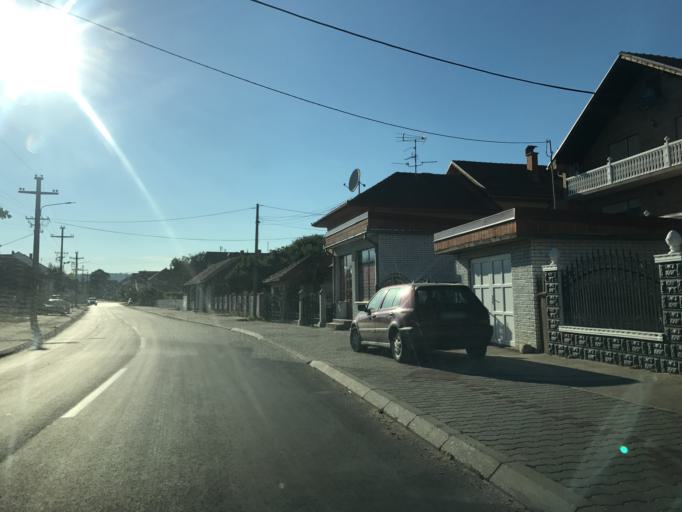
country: RS
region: Central Serbia
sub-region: Borski Okrug
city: Negotin
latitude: 44.2252
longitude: 22.5450
